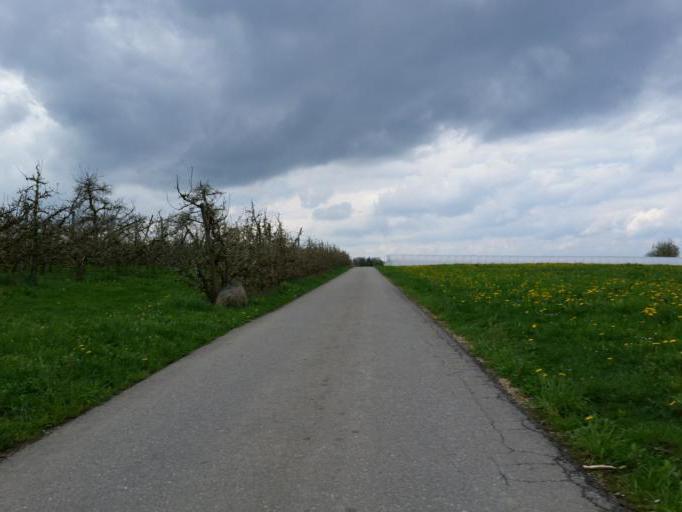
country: CH
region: Thurgau
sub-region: Arbon District
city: Uttwil
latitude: 47.5806
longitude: 9.3317
